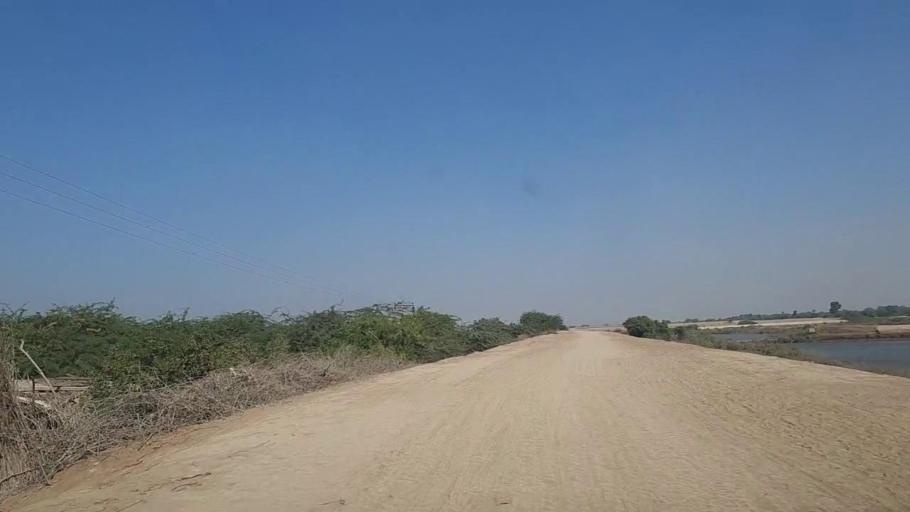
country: PK
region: Sindh
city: Daro Mehar
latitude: 24.8958
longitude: 68.0697
